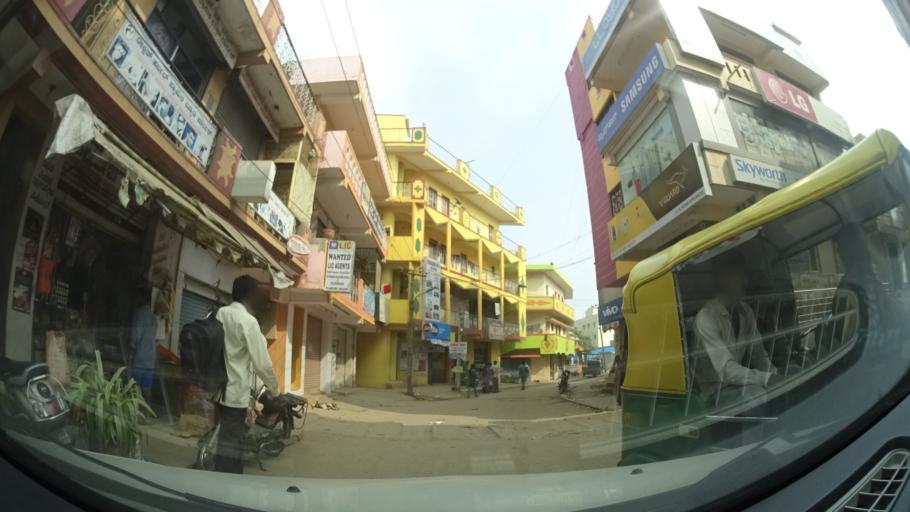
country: IN
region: Karnataka
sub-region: Bangalore Urban
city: Anekal
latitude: 12.8255
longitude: 77.6721
